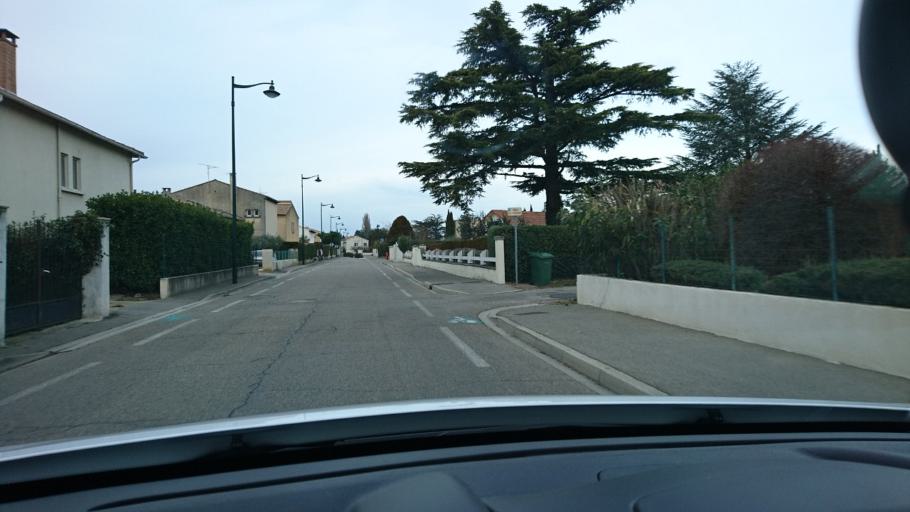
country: FR
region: Provence-Alpes-Cote d'Azur
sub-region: Departement des Bouches-du-Rhone
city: Rognonas
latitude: 43.9012
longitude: 4.8014
